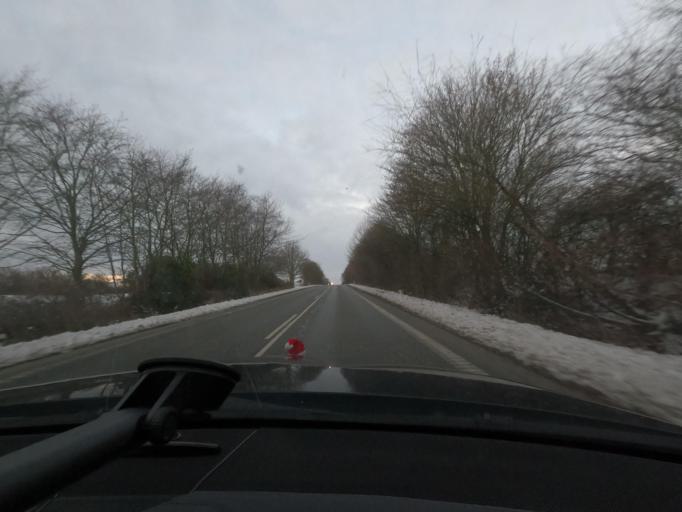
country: DE
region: Schleswig-Holstein
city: Glucksburg
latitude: 54.8901
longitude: 9.5337
